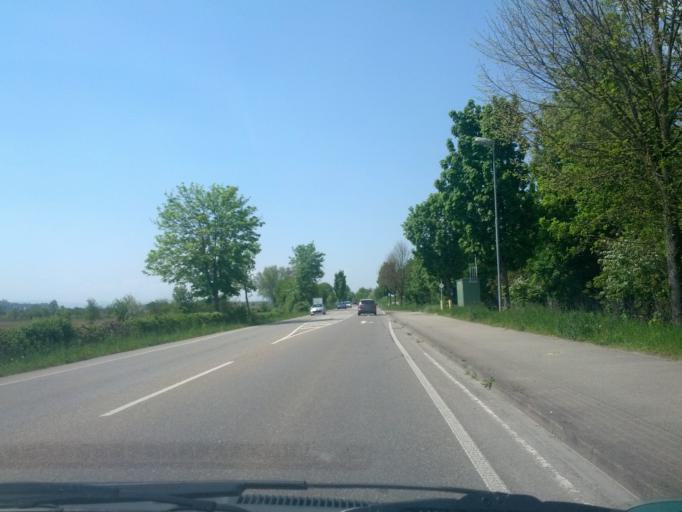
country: DE
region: Baden-Wuerttemberg
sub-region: Freiburg Region
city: Teningen
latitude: 48.1398
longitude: 7.8019
